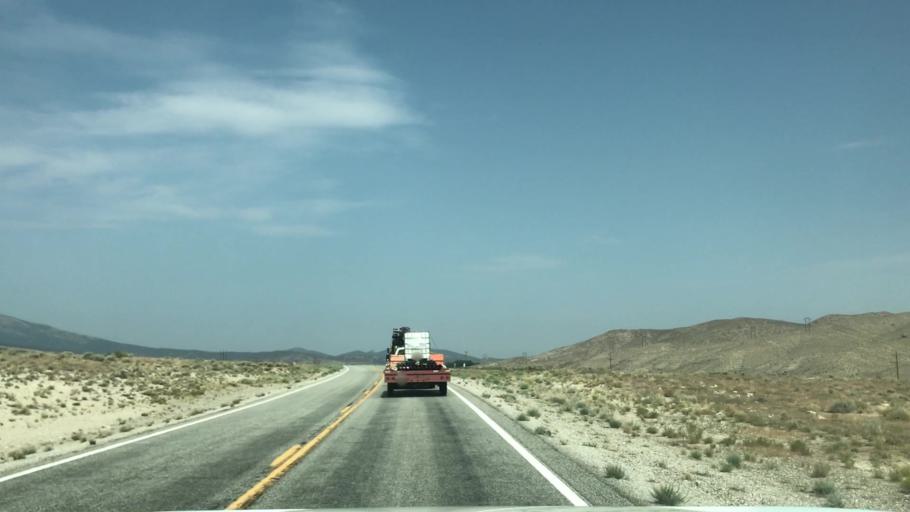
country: US
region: Nevada
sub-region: White Pine County
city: McGill
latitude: 39.0843
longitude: -114.2004
